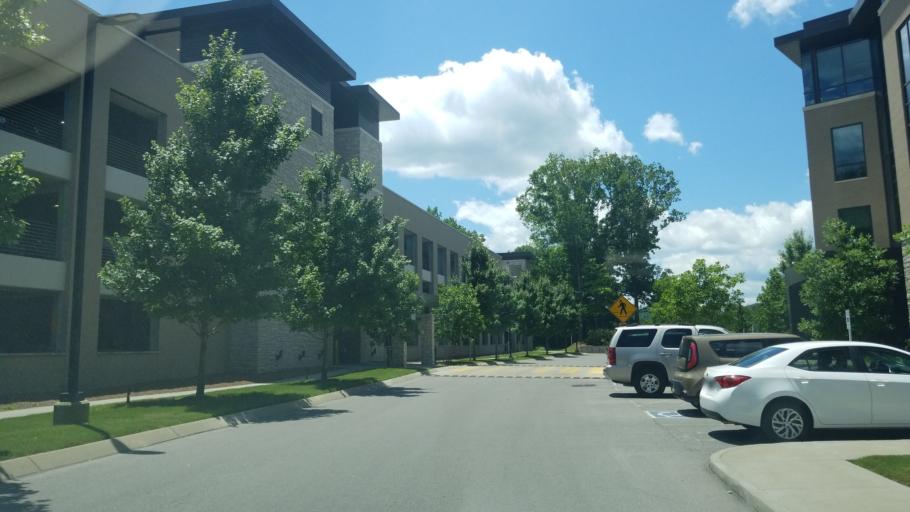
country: US
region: Tennessee
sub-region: Williamson County
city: Brentwood
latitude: 36.0320
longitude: -86.8124
